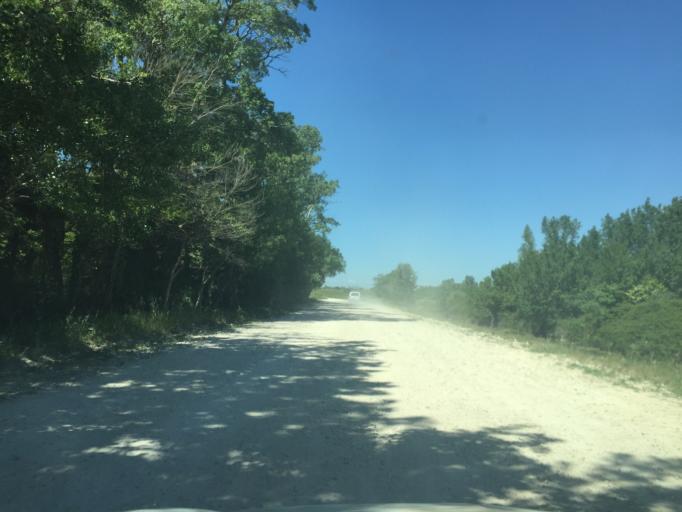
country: FR
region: Languedoc-Roussillon
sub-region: Departement du Gard
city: Roquemaure
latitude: 44.0533
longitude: 4.7932
